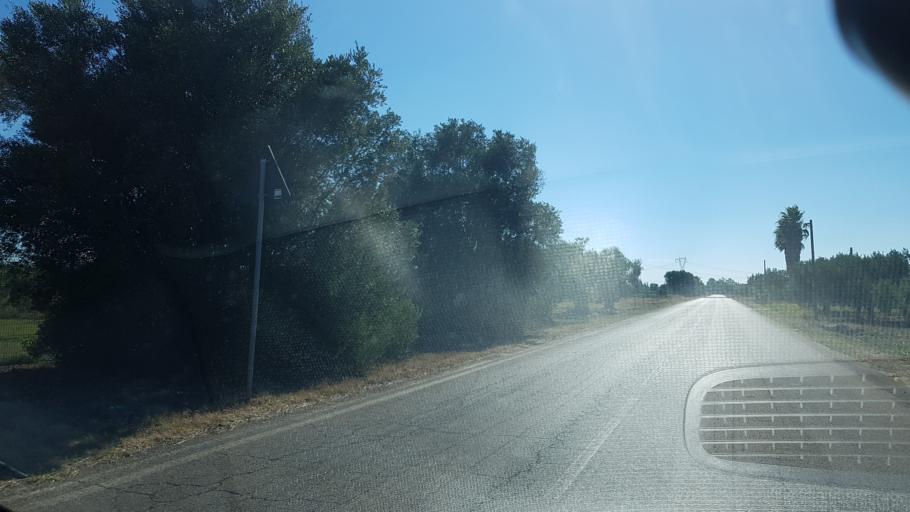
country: IT
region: Apulia
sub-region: Provincia di Brindisi
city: Tuturano
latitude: 40.5509
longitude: 17.8799
